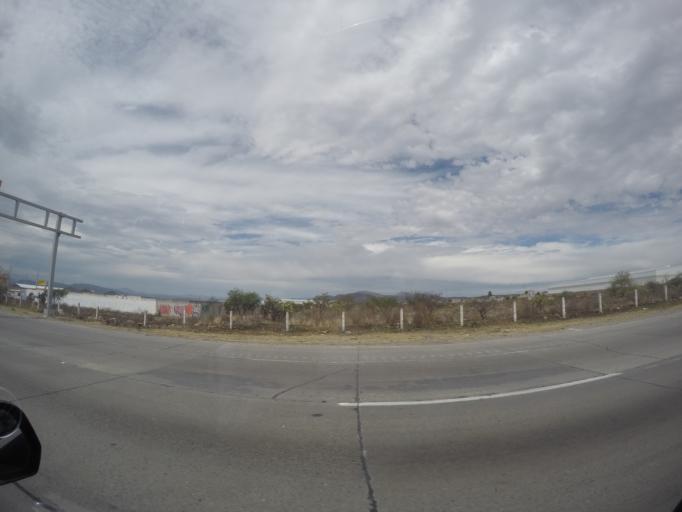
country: MX
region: Queretaro
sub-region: San Juan del Rio
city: Paso de Mata
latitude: 20.3564
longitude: -99.9592
